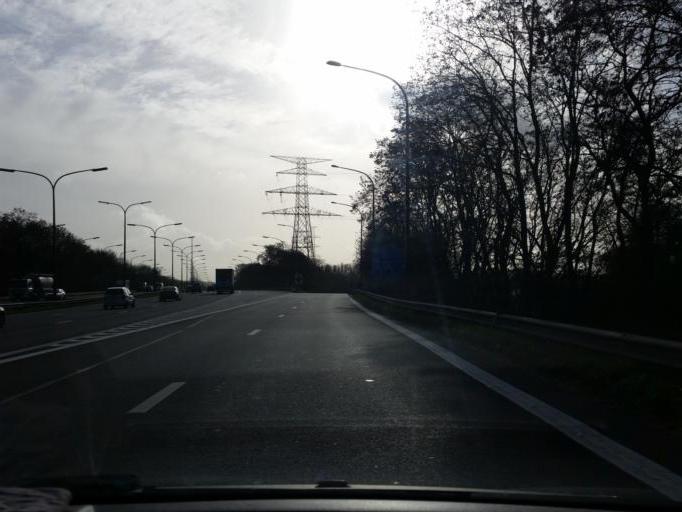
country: BE
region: Flanders
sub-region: Provincie Vlaams-Brabant
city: Drogenbos
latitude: 50.7953
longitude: 4.3042
